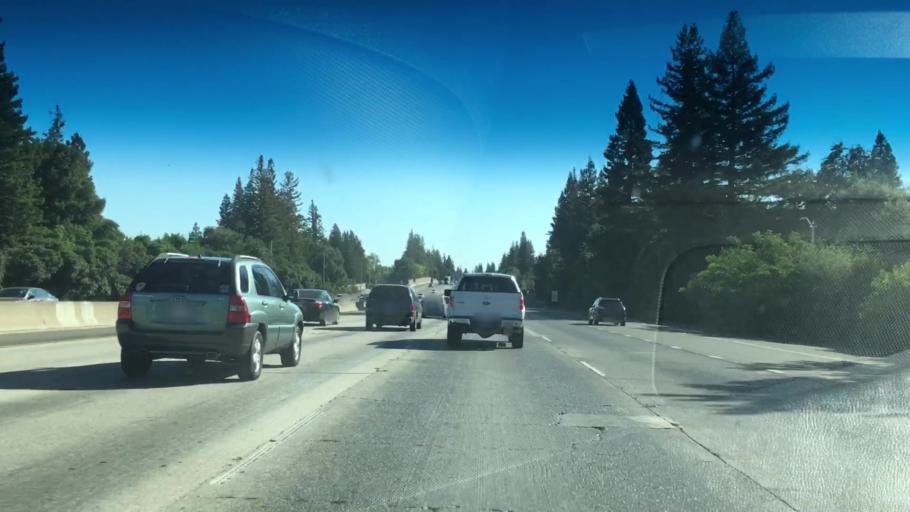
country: US
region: California
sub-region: Yolo County
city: West Sacramento
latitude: 38.5214
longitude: -121.5219
